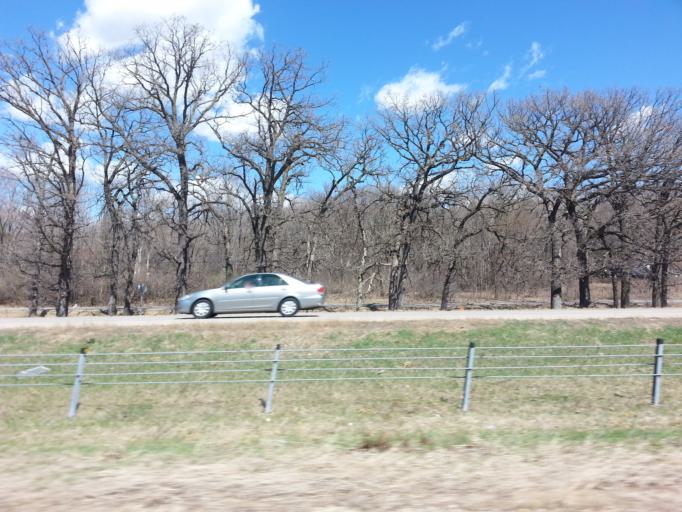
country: US
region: Minnesota
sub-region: Washington County
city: Cottage Grove
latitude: 44.7967
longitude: -92.8964
